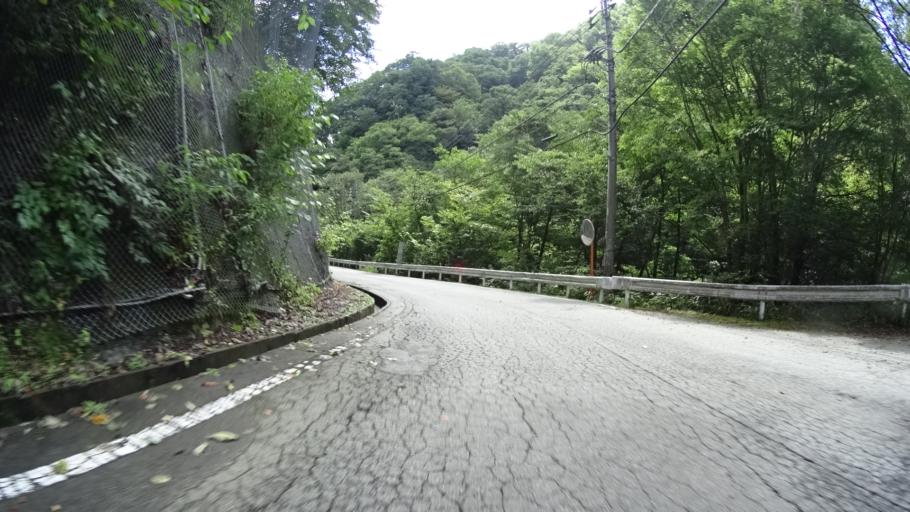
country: JP
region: Yamanashi
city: Enzan
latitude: 35.6744
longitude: 138.8065
